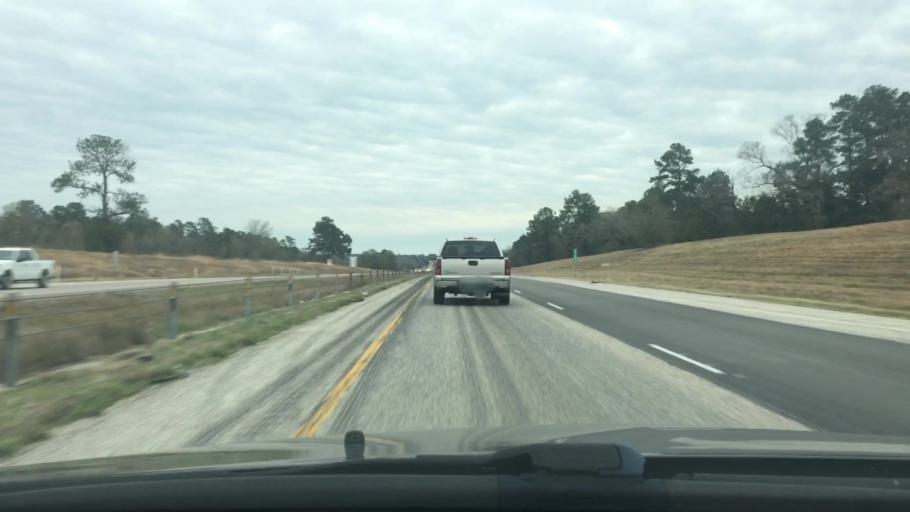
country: US
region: Texas
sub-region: Walker County
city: Huntsville
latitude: 30.7748
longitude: -95.6476
